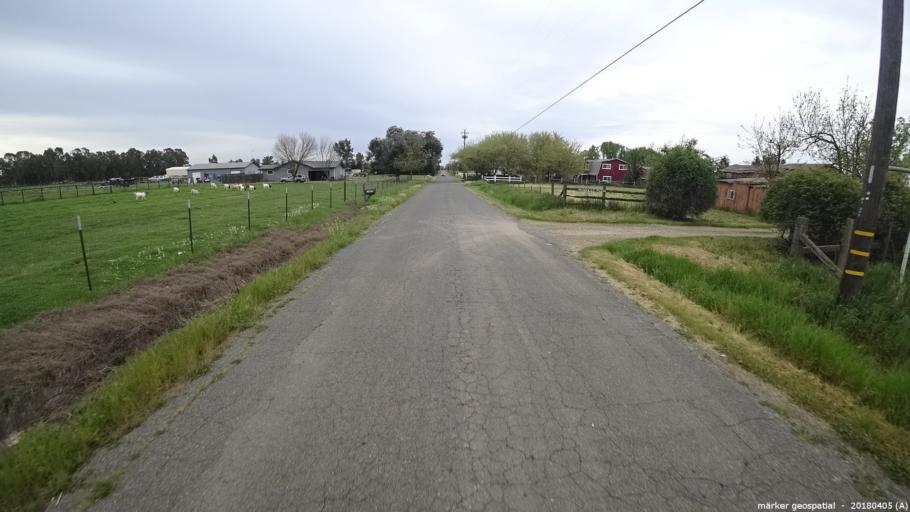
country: US
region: California
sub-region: Sacramento County
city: Herald
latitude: 38.2818
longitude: -121.2357
